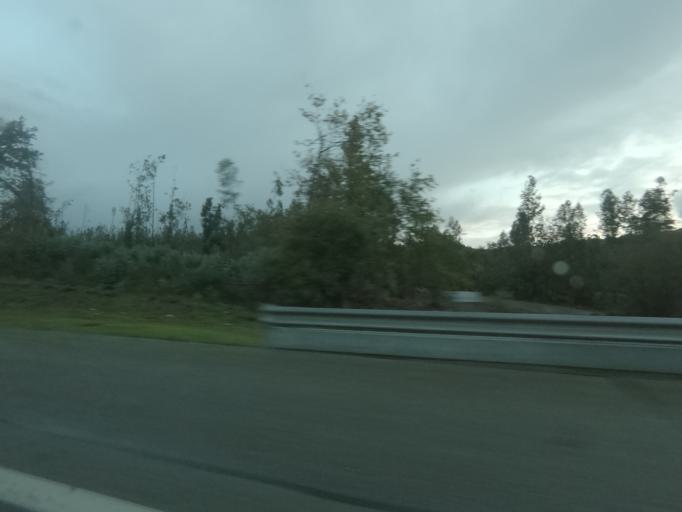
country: PT
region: Braga
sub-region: Vila Verde
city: Prado
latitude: 41.5450
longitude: -8.5005
